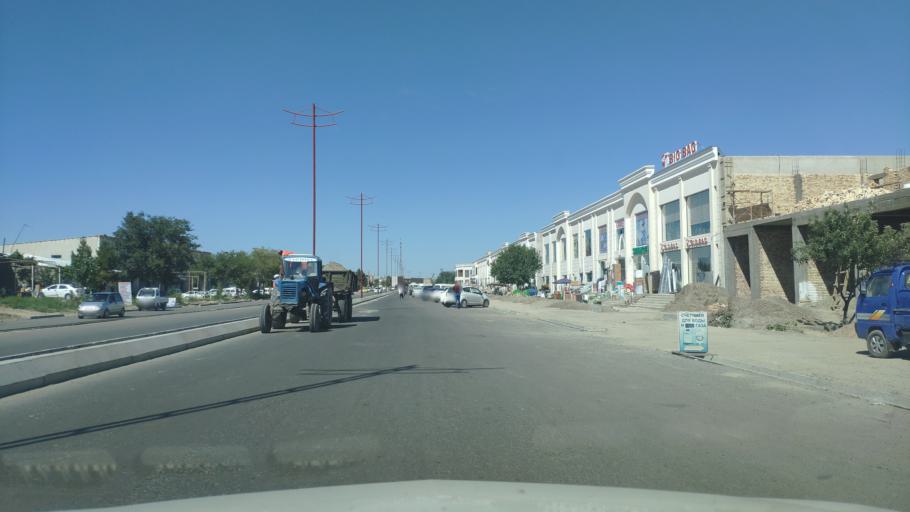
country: UZ
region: Bukhara
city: Bukhara
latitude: 39.7757
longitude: 64.3904
